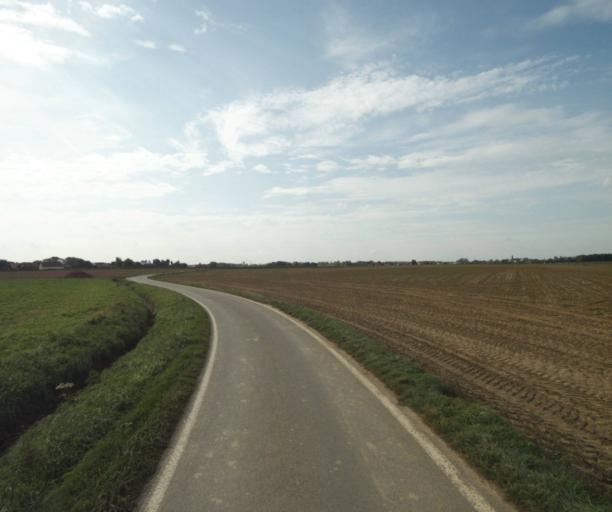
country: FR
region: Nord-Pas-de-Calais
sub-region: Departement du Nord
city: Salome
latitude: 50.5385
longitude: 2.8639
